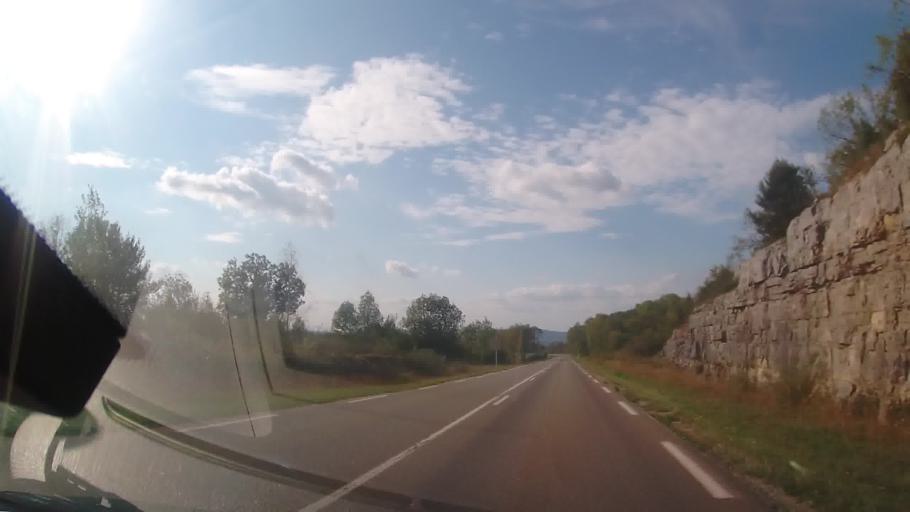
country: FR
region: Franche-Comte
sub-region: Departement du Jura
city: Clairvaux-les-Lacs
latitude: 46.5812
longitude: 5.7737
